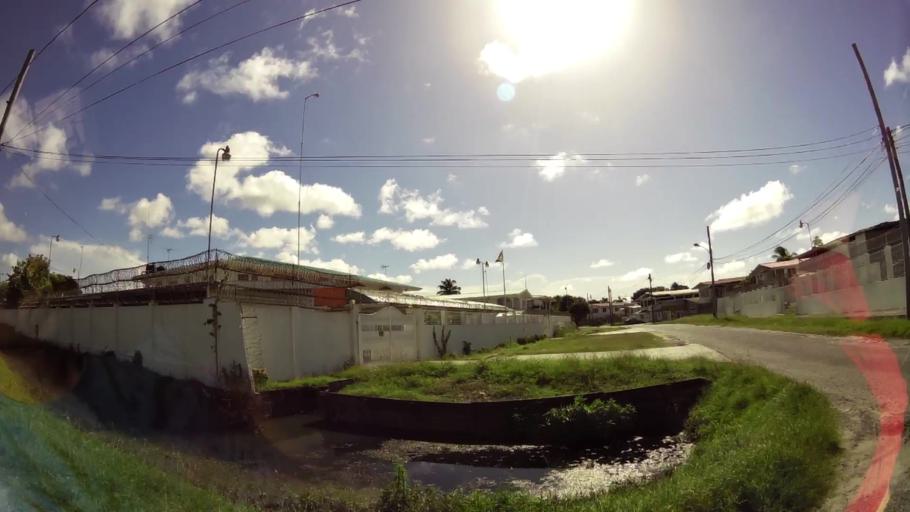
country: GY
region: Demerara-Mahaica
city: Georgetown
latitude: 6.8221
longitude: -58.1305
